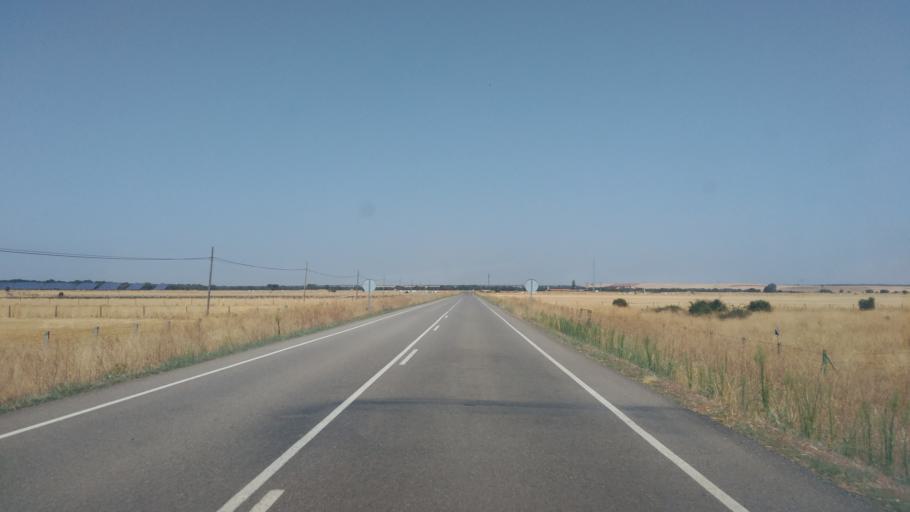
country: ES
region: Castille and Leon
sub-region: Provincia de Salamanca
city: Abusejo
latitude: 40.7139
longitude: -6.1447
